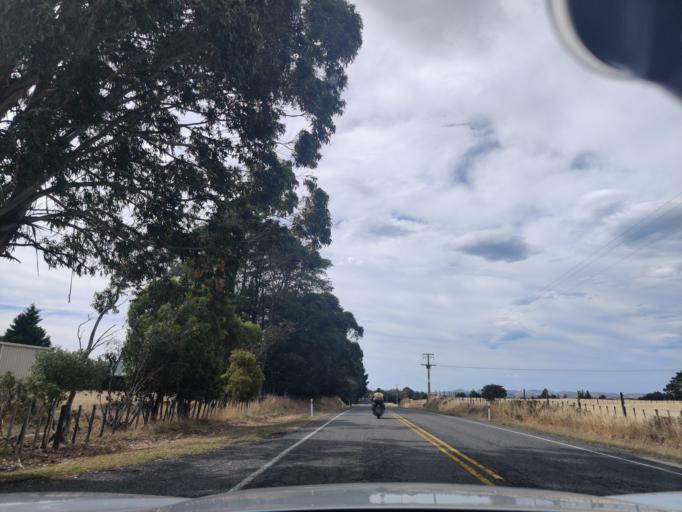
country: NZ
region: Wellington
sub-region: Masterton District
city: Masterton
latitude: -40.8752
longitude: 175.6524
